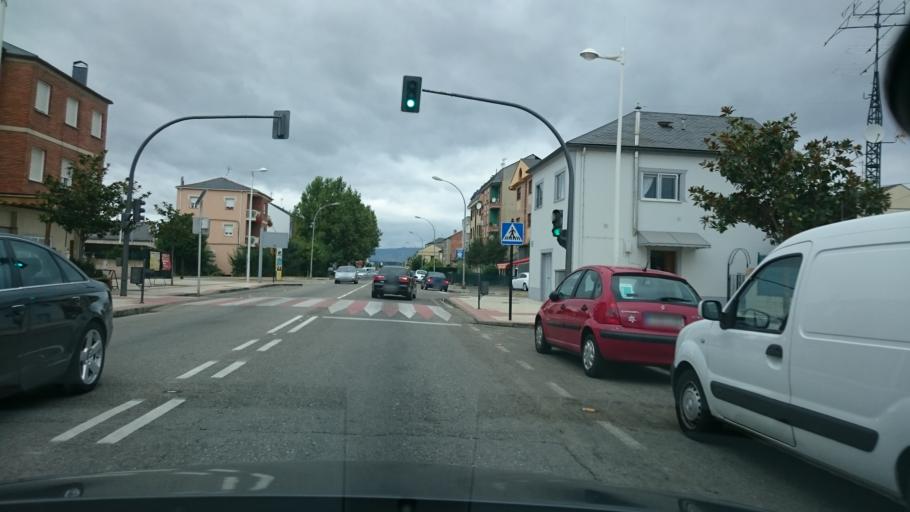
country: ES
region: Castille and Leon
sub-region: Provincia de Leon
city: Ponferrada
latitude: 42.5621
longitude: -6.6292
